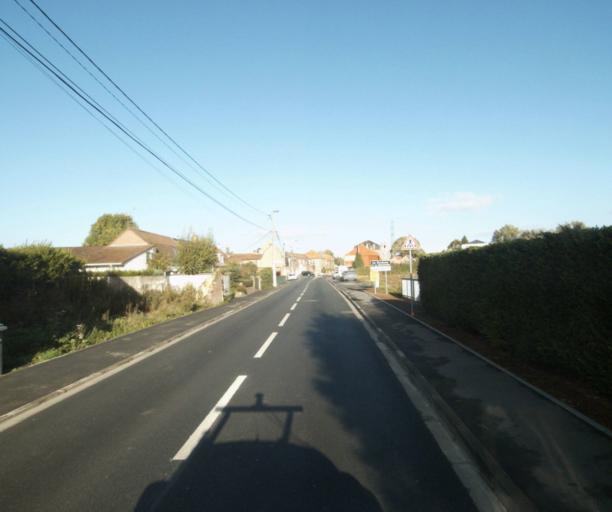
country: FR
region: Nord-Pas-de-Calais
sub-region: Departement du Nord
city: Verlinghem
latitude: 50.6718
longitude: 3.0210
